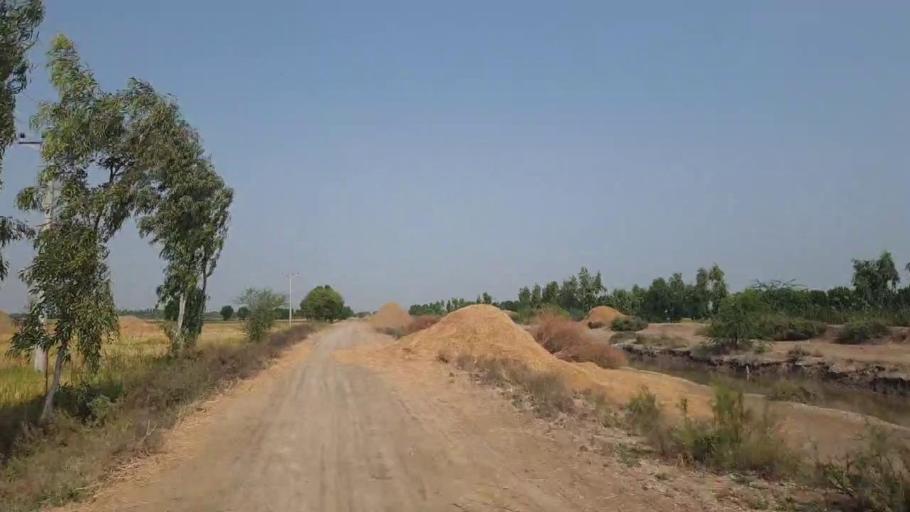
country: PK
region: Sindh
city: Badin
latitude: 24.7486
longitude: 68.7627
